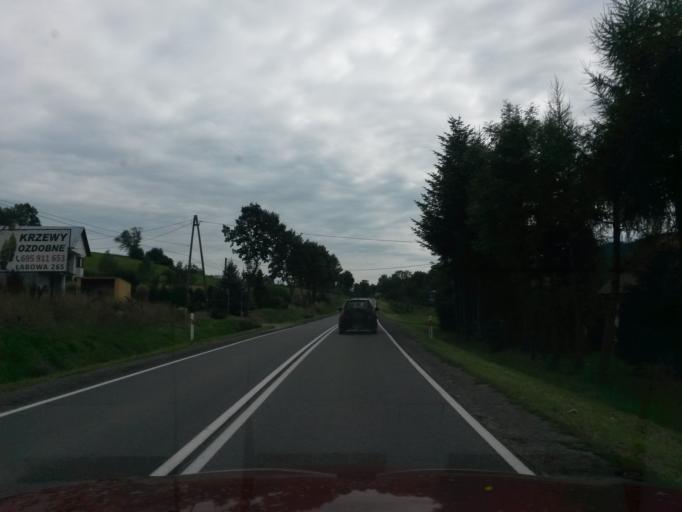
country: PL
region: Lesser Poland Voivodeship
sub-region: Powiat nowosadecki
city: Labowa
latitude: 49.5206
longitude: 20.8779
